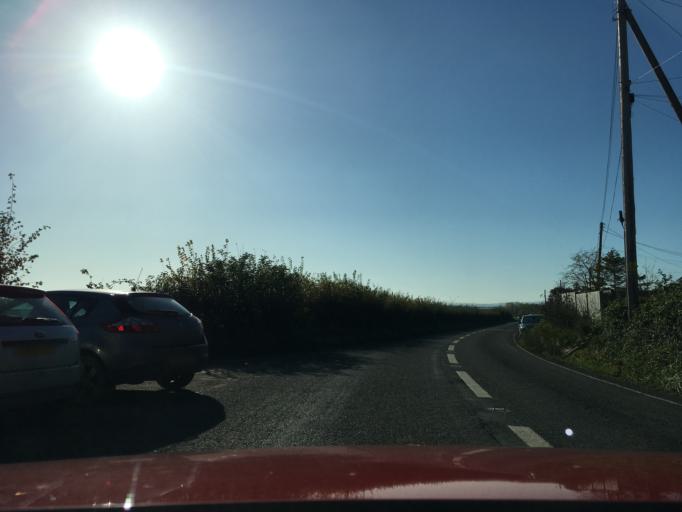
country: GB
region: England
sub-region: Somerset
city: Martock
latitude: 51.0013
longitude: -2.7650
